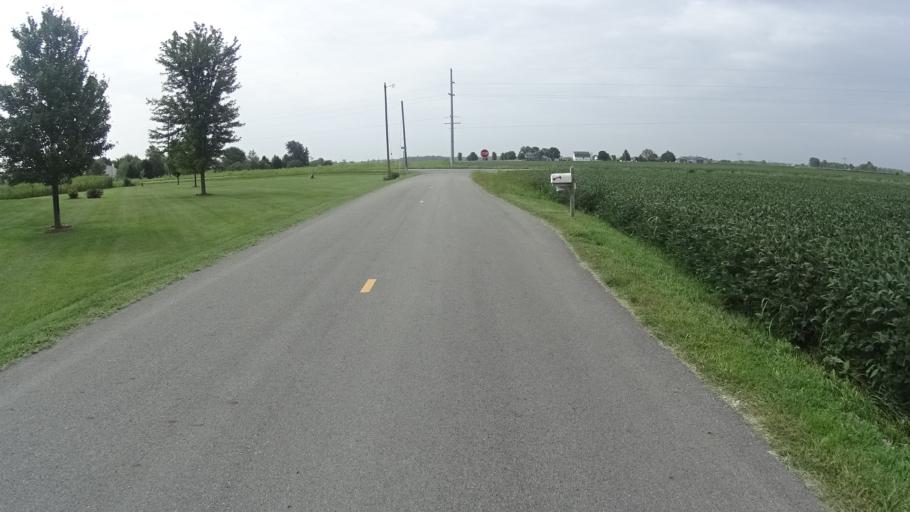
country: US
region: Indiana
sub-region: Madison County
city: Ingalls
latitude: 40.0125
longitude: -85.8055
